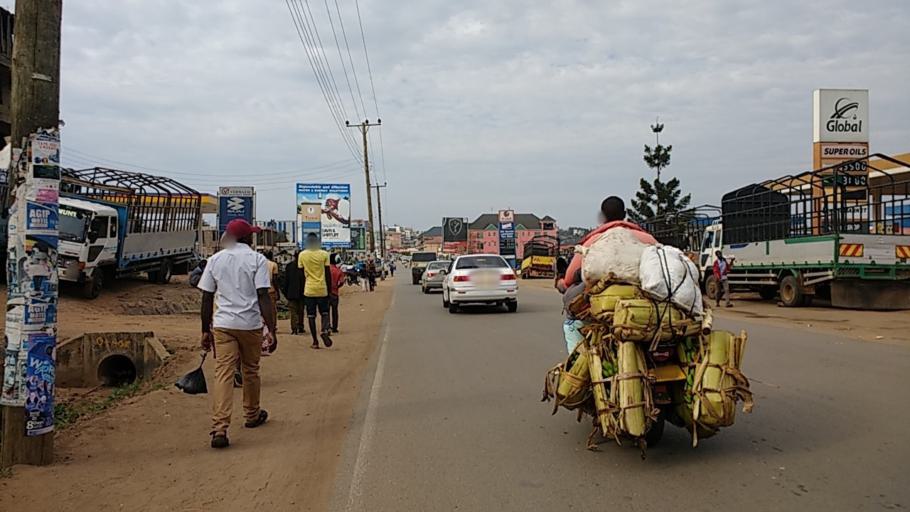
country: UG
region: Western Region
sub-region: Mbarara District
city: Mbarara
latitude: -0.5977
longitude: 30.6644
